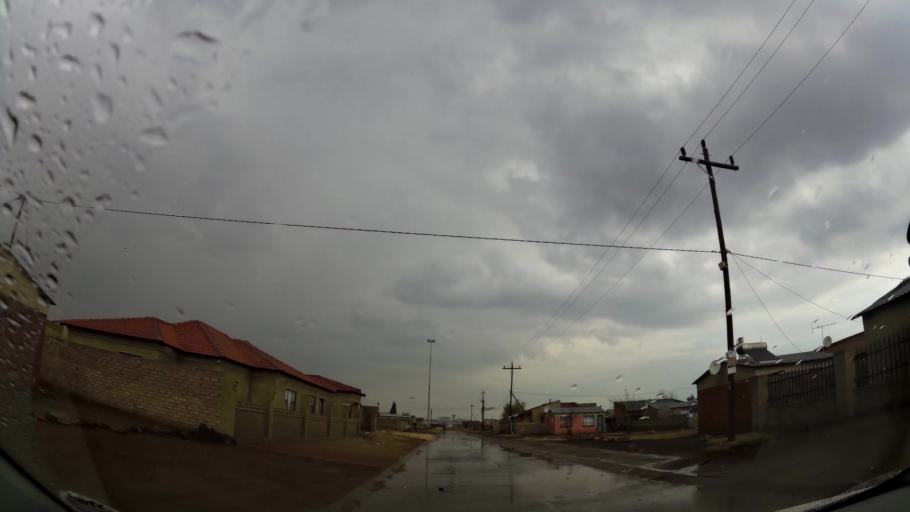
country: ZA
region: Gauteng
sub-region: Ekurhuleni Metropolitan Municipality
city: Germiston
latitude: -26.3736
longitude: 28.1472
